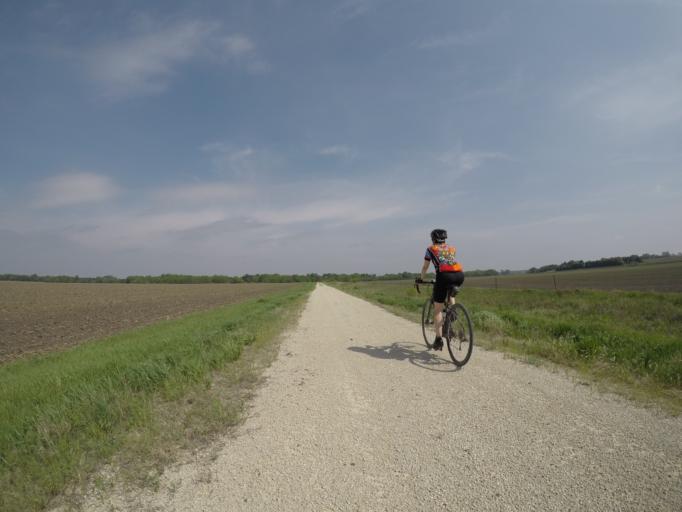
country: US
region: Nebraska
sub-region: Gage County
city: Wymore
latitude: 40.0653
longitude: -96.5808
